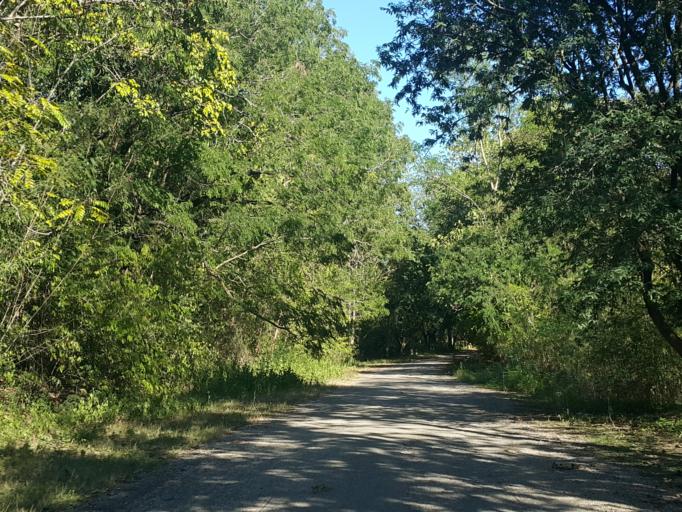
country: TH
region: Chiang Mai
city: San Sai
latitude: 18.9261
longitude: 99.1306
